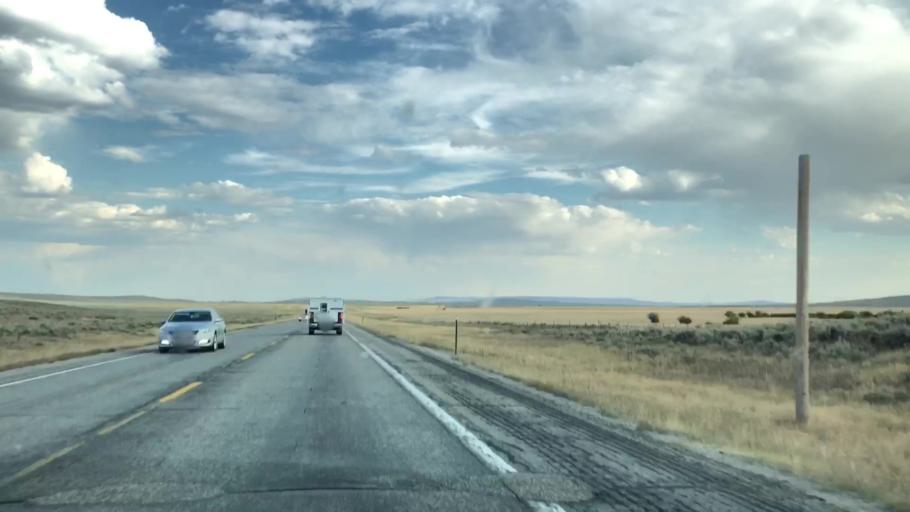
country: US
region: Wyoming
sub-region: Sublette County
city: Pinedale
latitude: 43.0450
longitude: -110.1454
